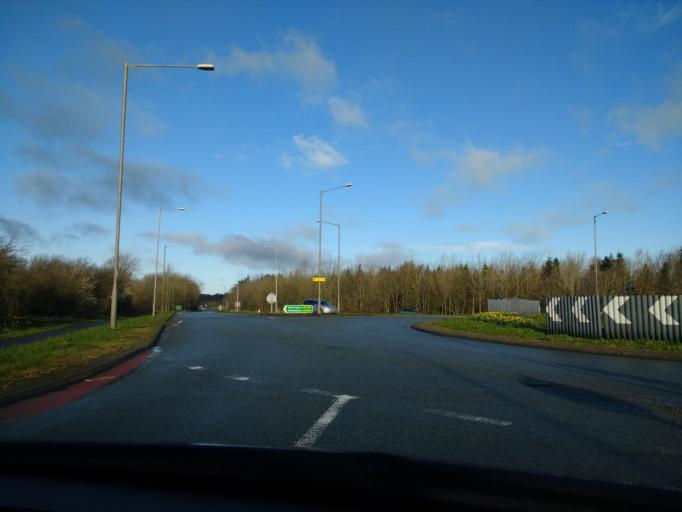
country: GB
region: England
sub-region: Cumbria
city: Cockermouth
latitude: 54.6660
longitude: -3.3944
